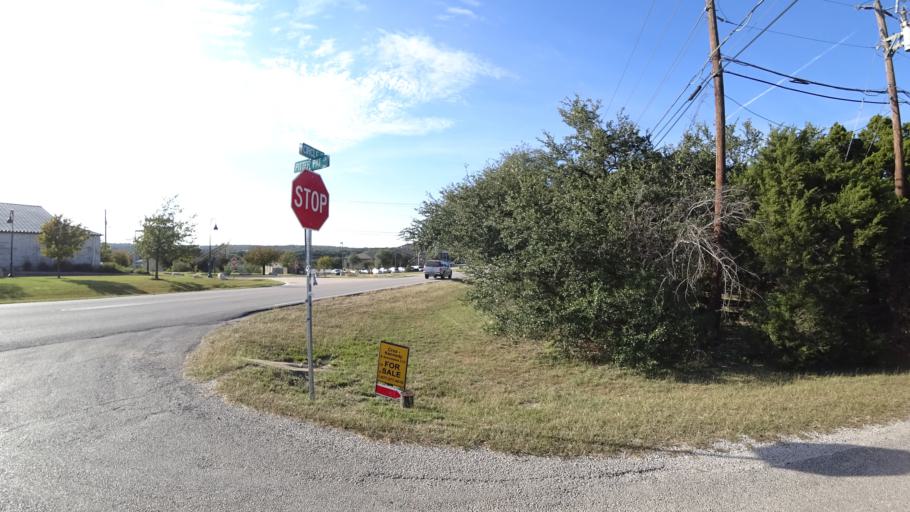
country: US
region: Texas
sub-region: Travis County
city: Barton Creek
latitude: 30.2388
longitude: -97.9182
